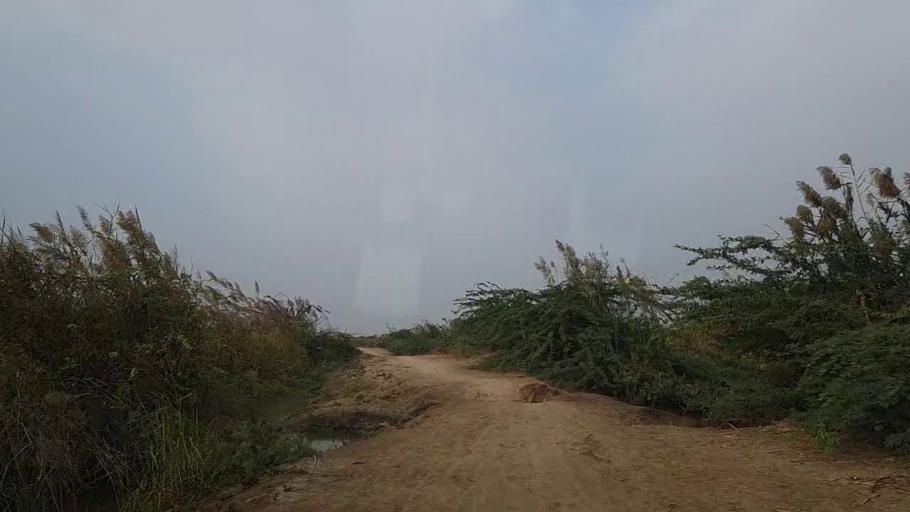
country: PK
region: Sindh
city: Mirpur Sakro
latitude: 24.6208
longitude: 67.5023
